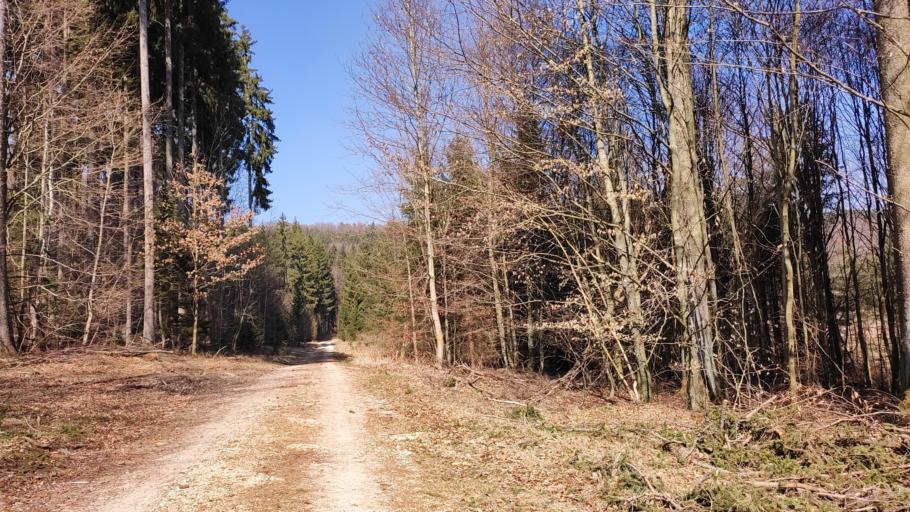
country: DE
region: Baden-Wuerttemberg
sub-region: Tuebingen Region
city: Borslingen
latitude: 48.5245
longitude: 10.0488
